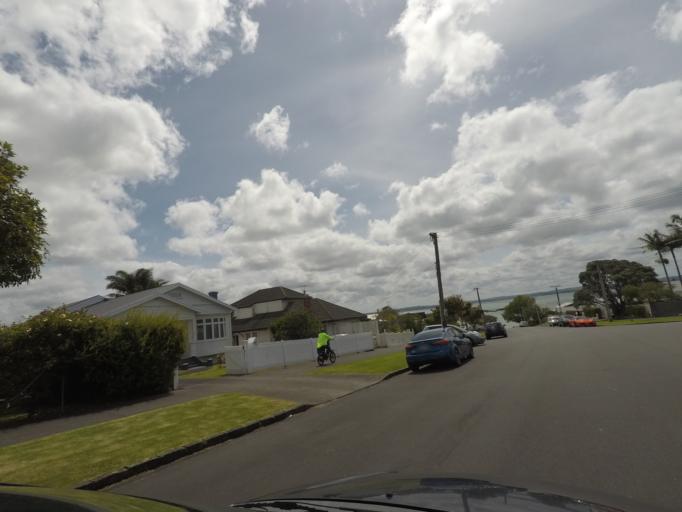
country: NZ
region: Auckland
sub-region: Auckland
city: Auckland
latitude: -36.8532
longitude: 174.7173
